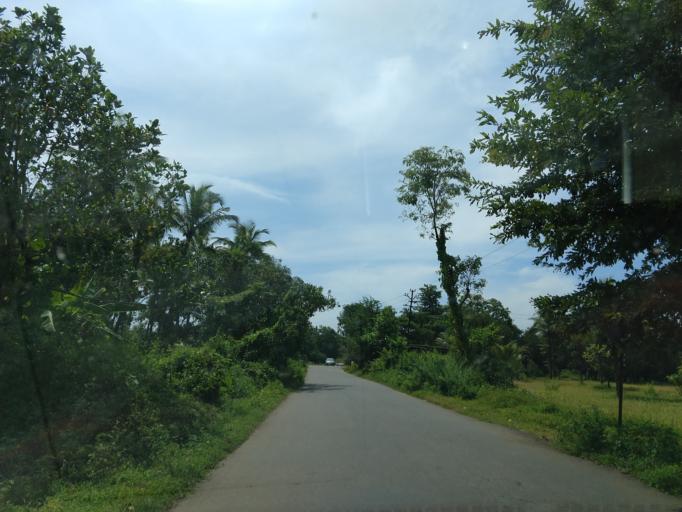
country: IN
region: Maharashtra
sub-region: Sindhudurg
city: Savantvadi
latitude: 15.9675
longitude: 73.7729
